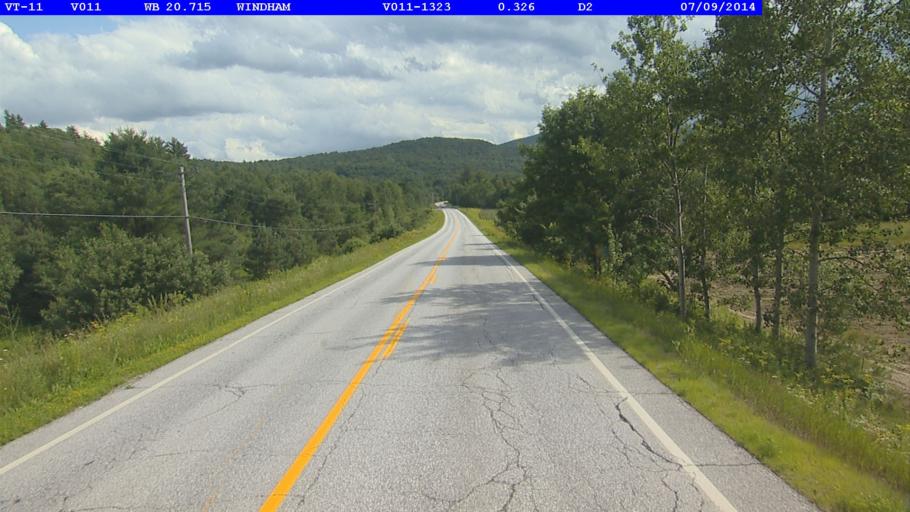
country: US
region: Vermont
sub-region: Windsor County
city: Chester
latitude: 43.2320
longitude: -72.7271
